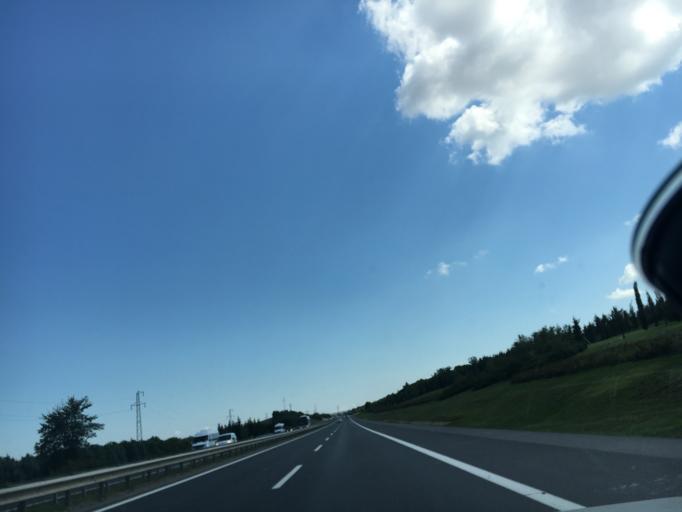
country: TR
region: Istanbul
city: Canta
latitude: 41.0798
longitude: 28.1281
